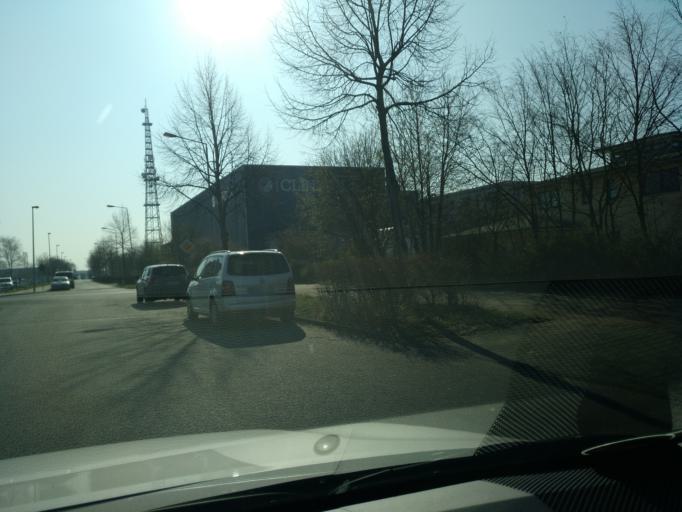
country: DE
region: Berlin
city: Mahlsdorf
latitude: 52.5095
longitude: 13.6334
